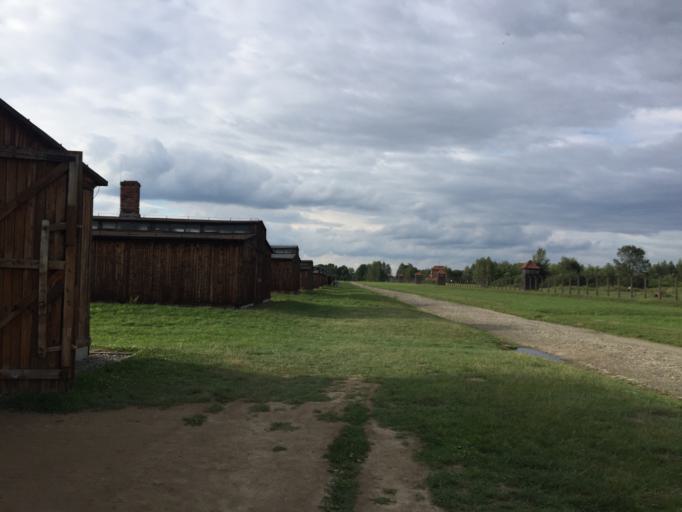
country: PL
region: Lesser Poland Voivodeship
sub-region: Powiat oswiecimski
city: Brzezinka
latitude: 50.0364
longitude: 19.1804
